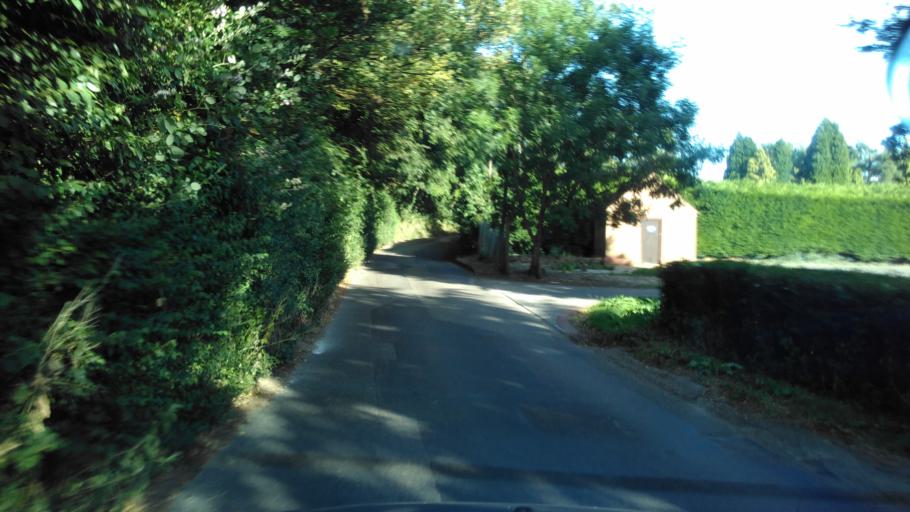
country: GB
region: England
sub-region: Kent
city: Dunkirk
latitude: 51.2887
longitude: 0.9366
